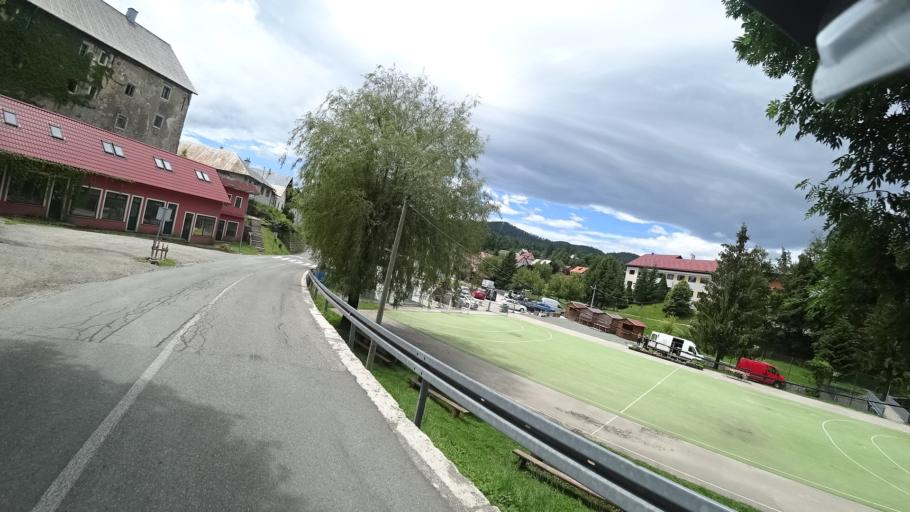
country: HR
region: Primorsko-Goranska
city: Hreljin
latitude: 45.3059
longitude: 14.7140
